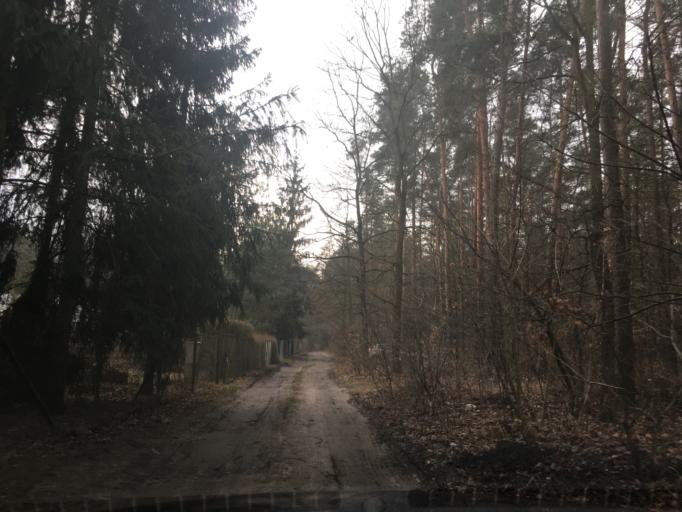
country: PL
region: Masovian Voivodeship
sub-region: Powiat piaseczynski
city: Lesznowola
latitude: 52.0786
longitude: 20.9194
